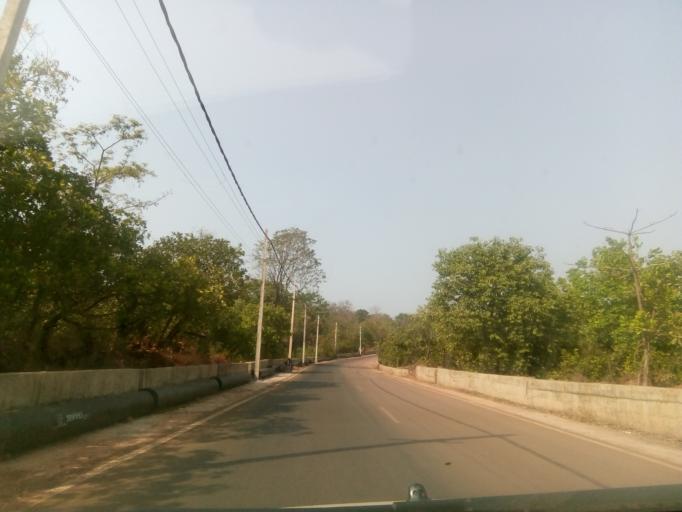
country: IN
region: Goa
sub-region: North Goa
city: Pernem
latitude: 15.7257
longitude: 73.8550
